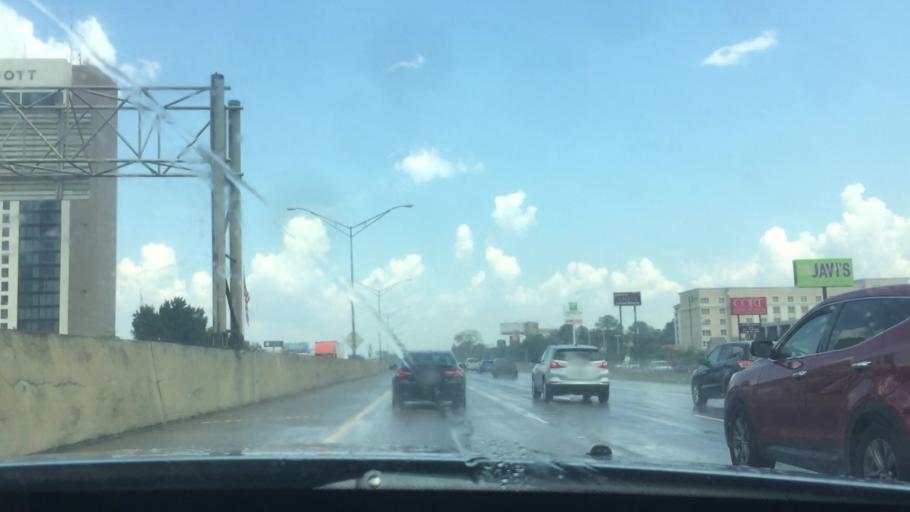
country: US
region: Louisiana
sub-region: East Baton Rouge Parish
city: Baton Rouge
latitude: 30.4227
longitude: -91.1364
